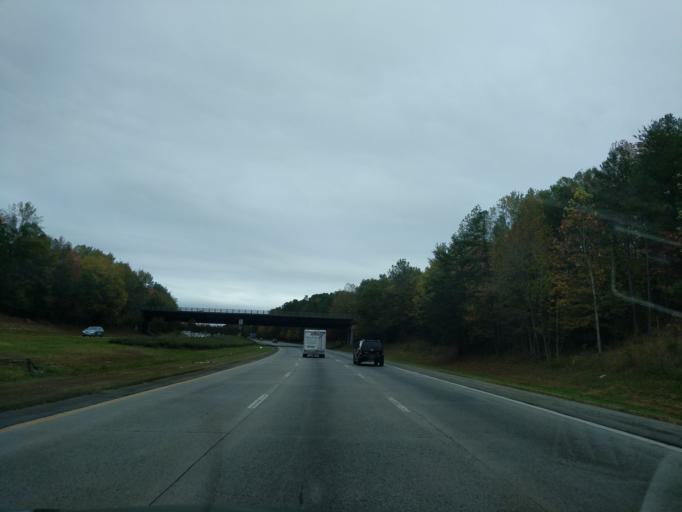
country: US
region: North Carolina
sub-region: Davidson County
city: Thomasville
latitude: 35.8550
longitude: -80.0927
